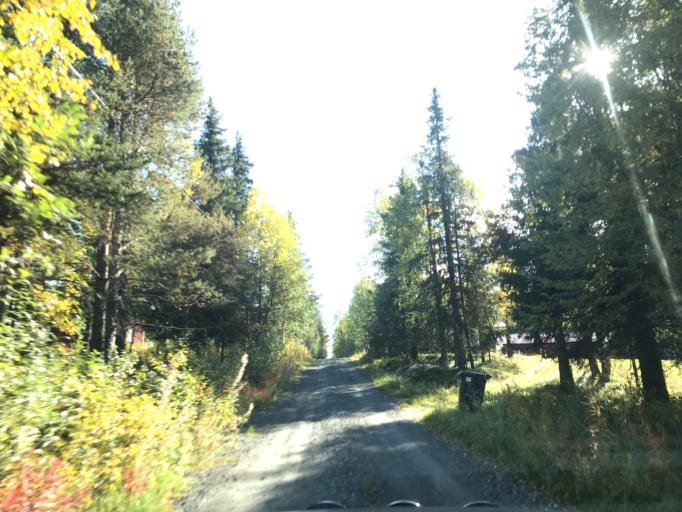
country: SE
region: Norrbotten
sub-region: Gallivare Kommun
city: Malmberget
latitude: 67.6457
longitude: 21.0658
